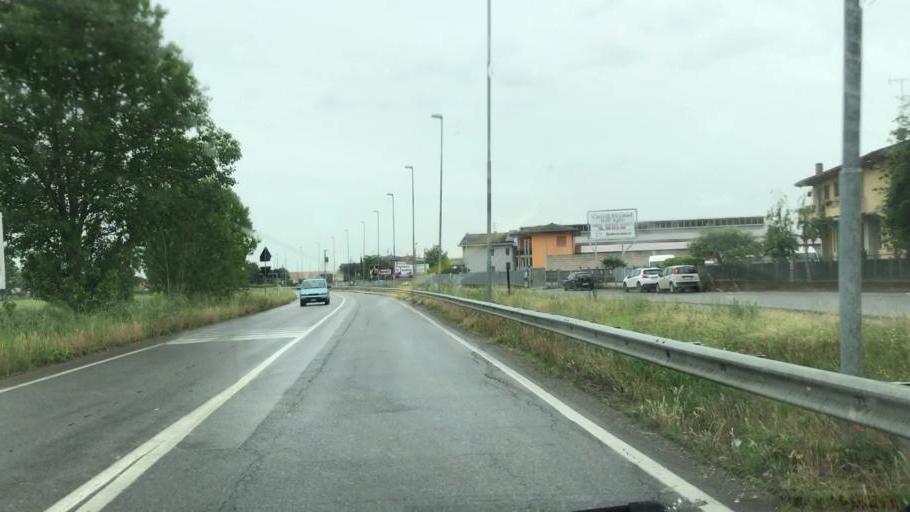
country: IT
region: Lombardy
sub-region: Provincia di Brescia
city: Montichiari
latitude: 45.3979
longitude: 10.3985
